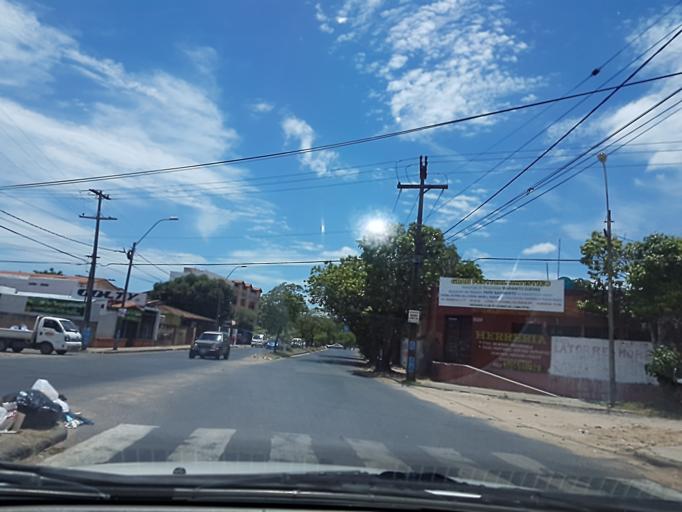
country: PY
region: Asuncion
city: Asuncion
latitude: -25.2561
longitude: -57.5778
